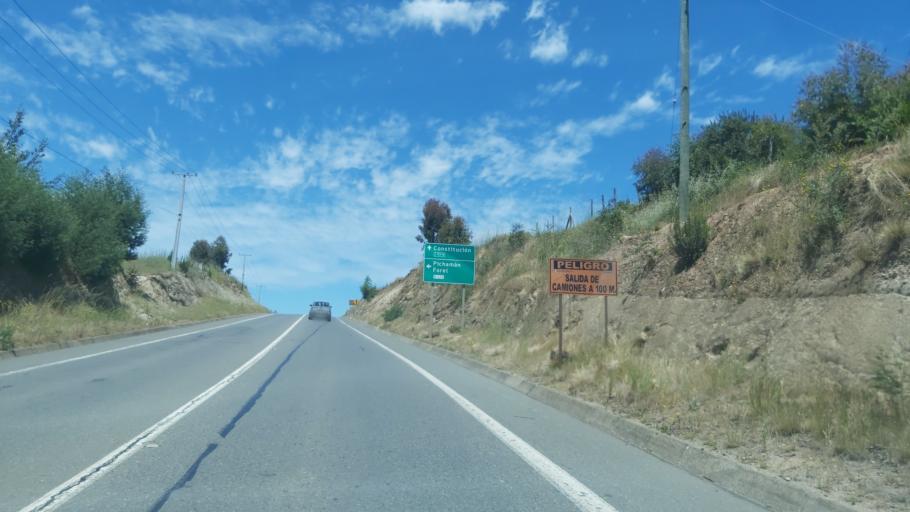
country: CL
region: Maule
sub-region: Provincia de Talca
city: Constitucion
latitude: -35.3165
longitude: -72.3854
